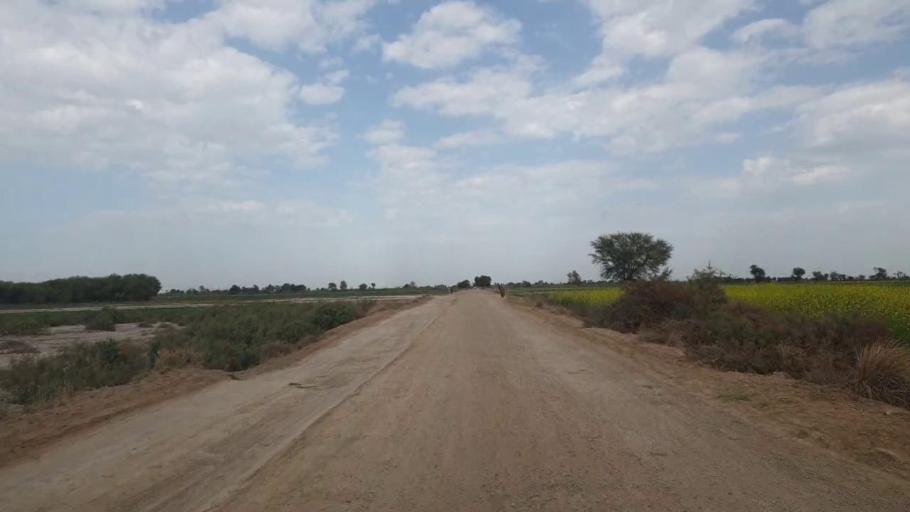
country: PK
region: Sindh
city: Hala
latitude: 25.9605
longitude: 68.4671
